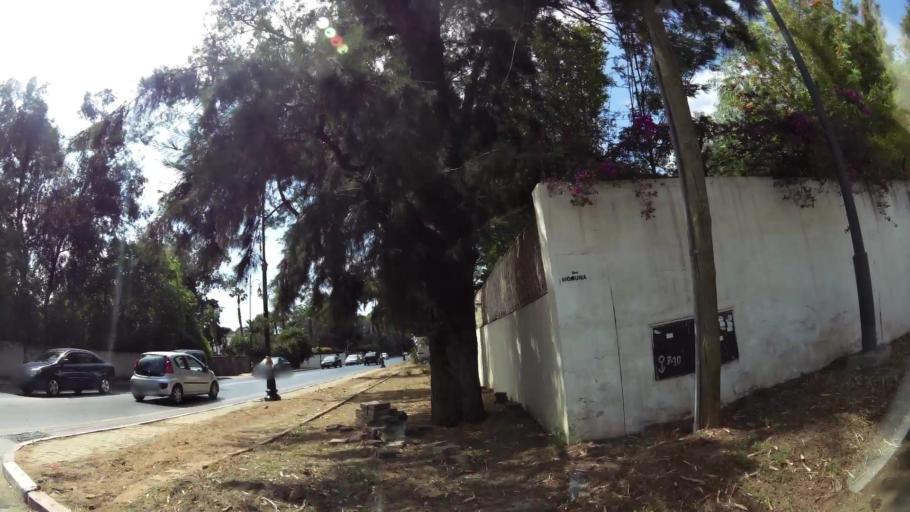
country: MA
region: Rabat-Sale-Zemmour-Zaer
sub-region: Rabat
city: Rabat
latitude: 33.9807
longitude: -6.8435
